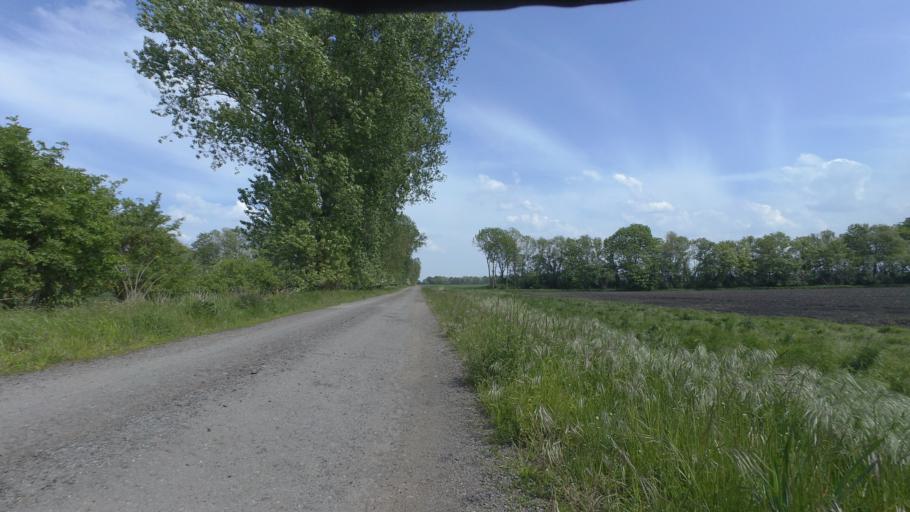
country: DE
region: Lower Saxony
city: Jerxheim
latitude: 52.0621
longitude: 10.8968
